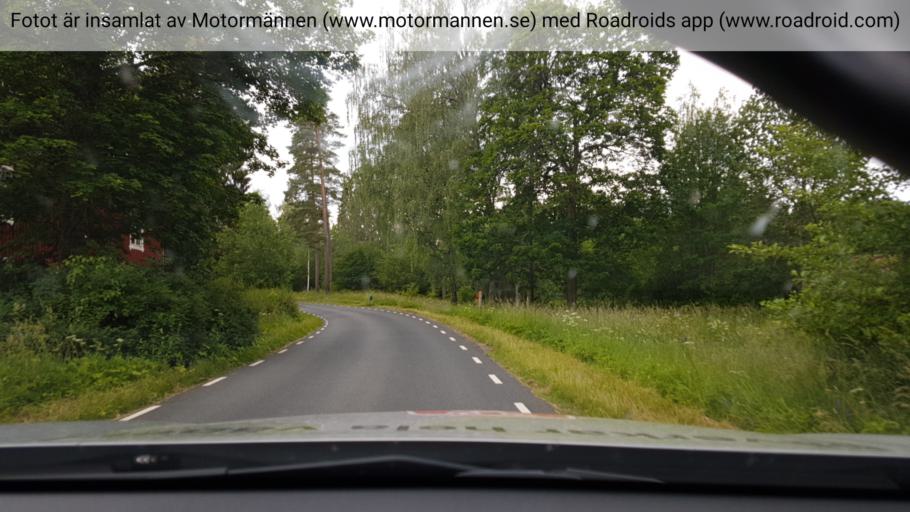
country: SE
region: Joenkoeping
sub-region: Mullsjo Kommun
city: Mullsjoe
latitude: 57.9041
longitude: 13.8334
